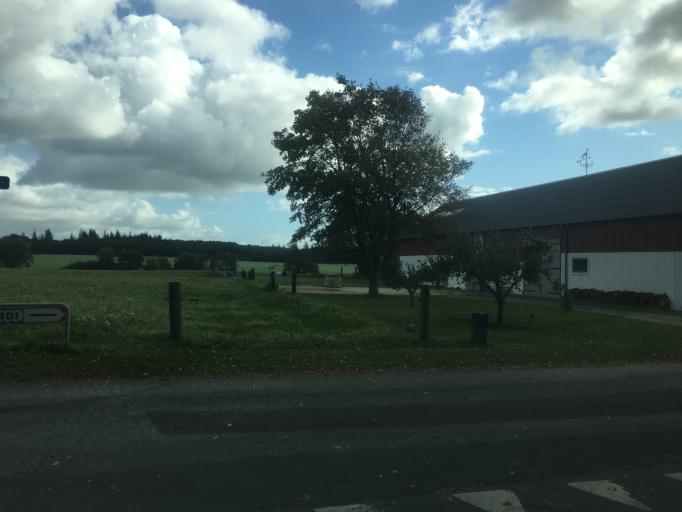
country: DK
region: South Denmark
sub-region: Tonder Kommune
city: Logumkloster
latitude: 55.1138
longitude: 8.8835
